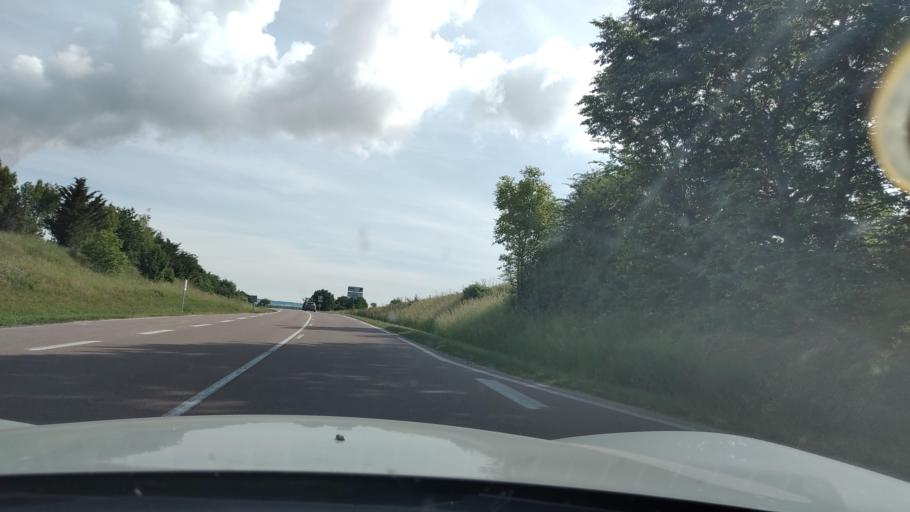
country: FR
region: Champagne-Ardenne
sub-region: Departement de l'Aube
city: Nogent-sur-Seine
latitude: 48.4872
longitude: 3.5187
